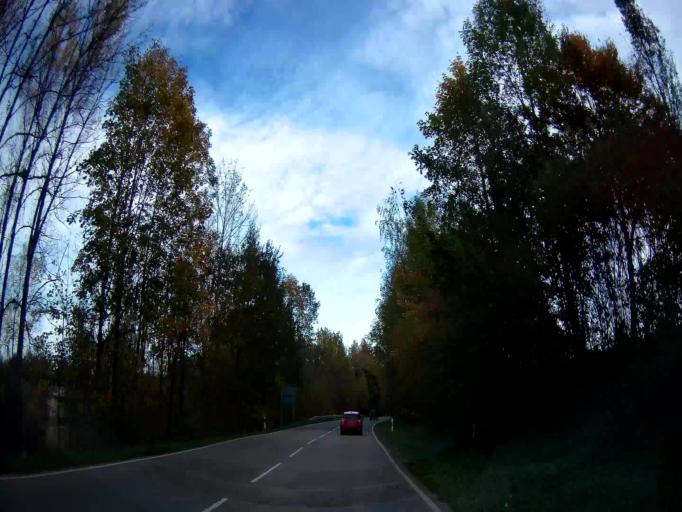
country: DE
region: Bavaria
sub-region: Upper Bavaria
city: Piding
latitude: 47.7621
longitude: 12.9252
